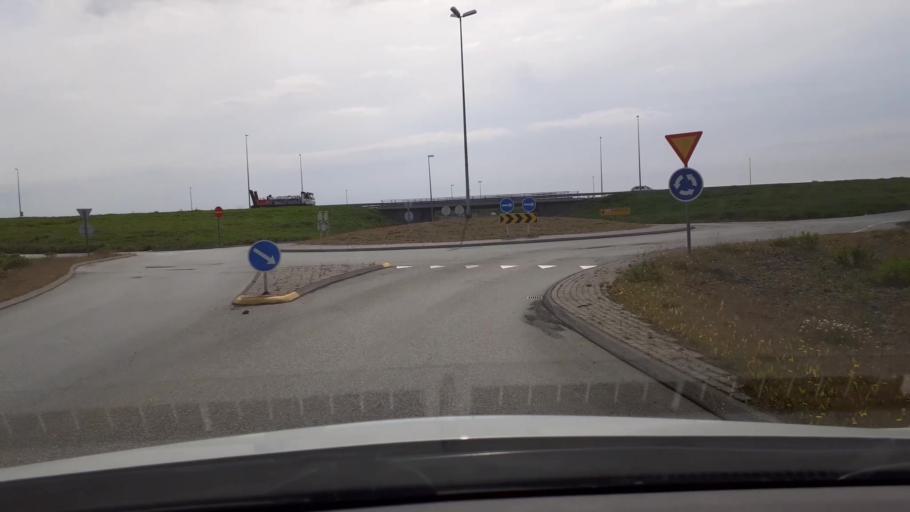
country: IS
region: Southern Peninsula
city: Reykjanesbaer
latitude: 63.9702
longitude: -22.5126
